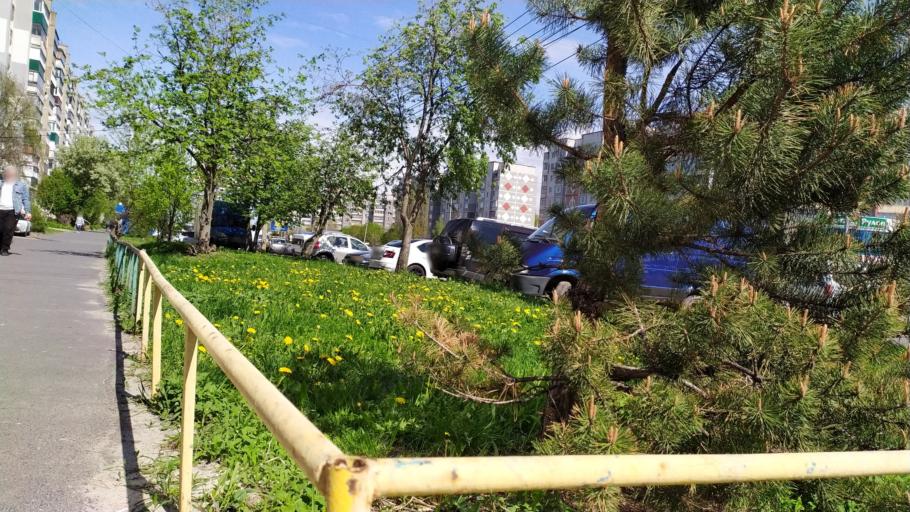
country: RU
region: Kursk
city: Kursk
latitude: 51.7379
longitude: 36.1371
